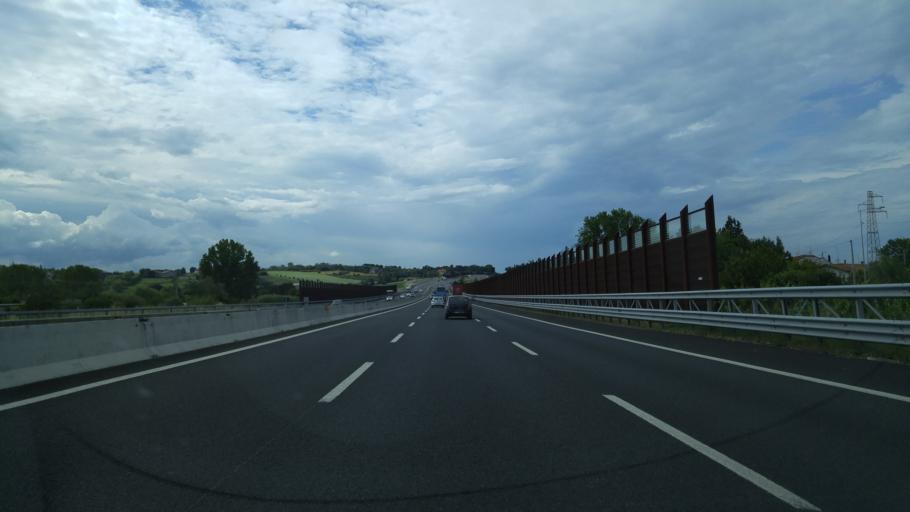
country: IT
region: Emilia-Romagna
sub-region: Provincia di Rimini
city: Rivazzurra
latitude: 44.0107
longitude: 12.5943
